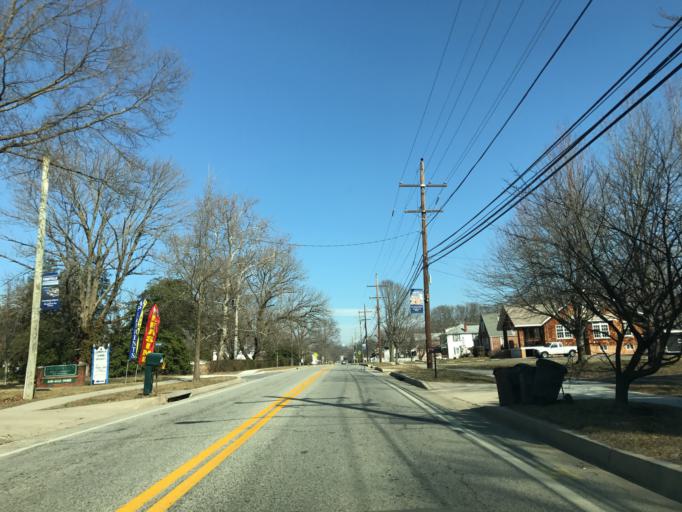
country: US
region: Maryland
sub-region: Cecil County
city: Perryville
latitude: 39.5629
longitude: -76.0712
